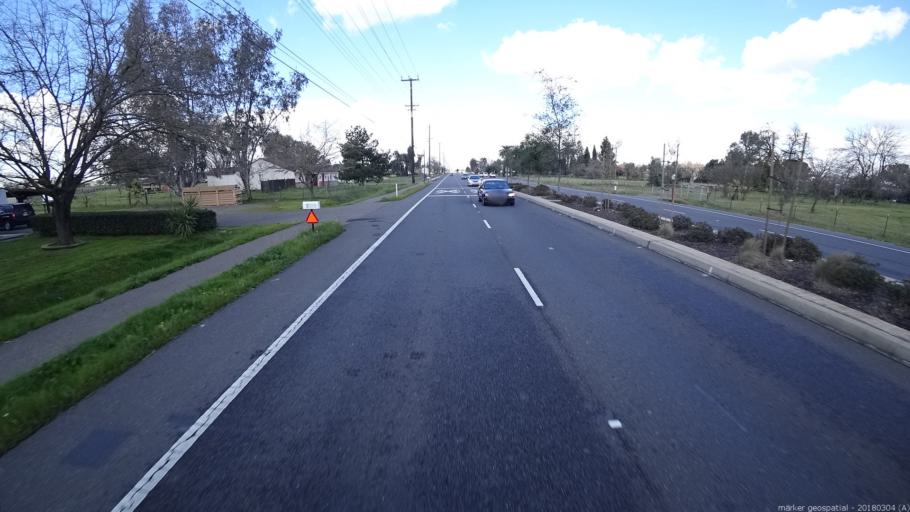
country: US
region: California
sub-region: Sacramento County
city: Vineyard
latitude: 38.4714
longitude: -121.3349
